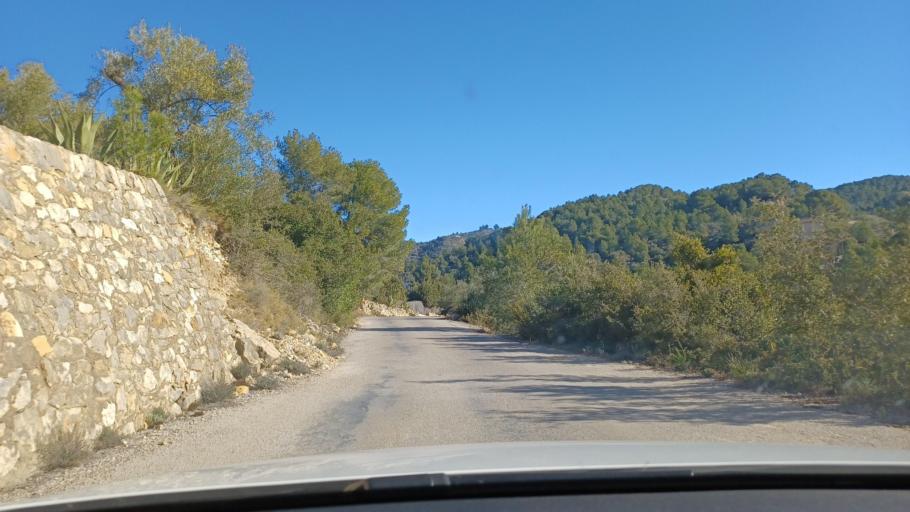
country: ES
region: Catalonia
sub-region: Provincia de Tarragona
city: Tortosa
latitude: 40.8151
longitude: 0.5582
